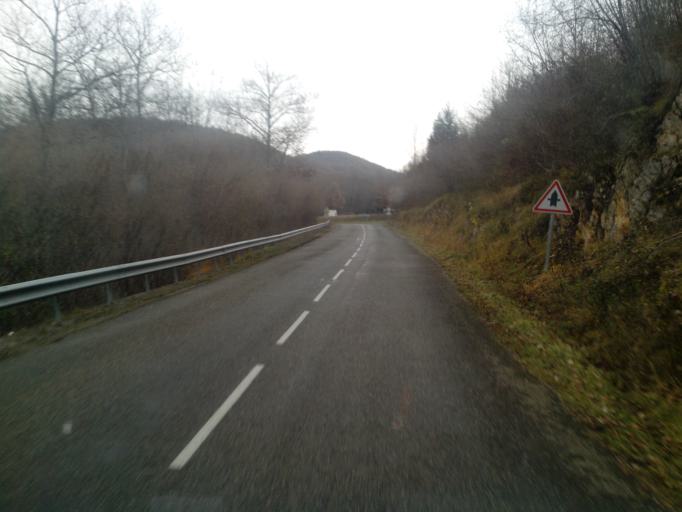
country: FR
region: Midi-Pyrenees
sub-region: Departement de l'Ariege
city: Foix
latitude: 43.0180
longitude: 1.5276
